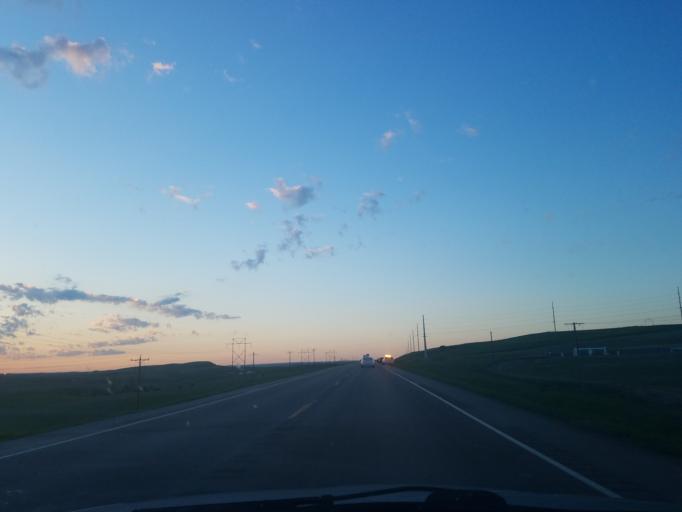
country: US
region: North Dakota
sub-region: McKenzie County
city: Watford City
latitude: 47.7006
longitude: -103.2833
